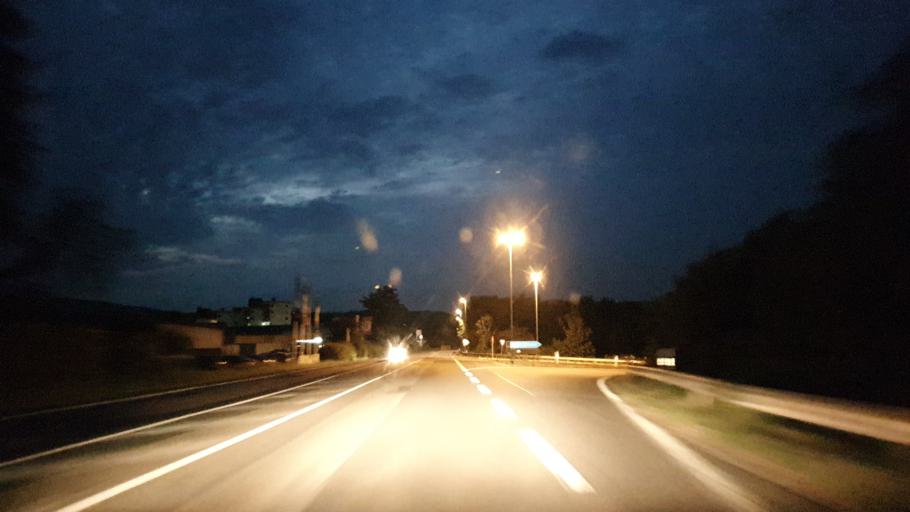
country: DE
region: Rheinland-Pfalz
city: Andernach
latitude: 50.4182
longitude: 7.4086
